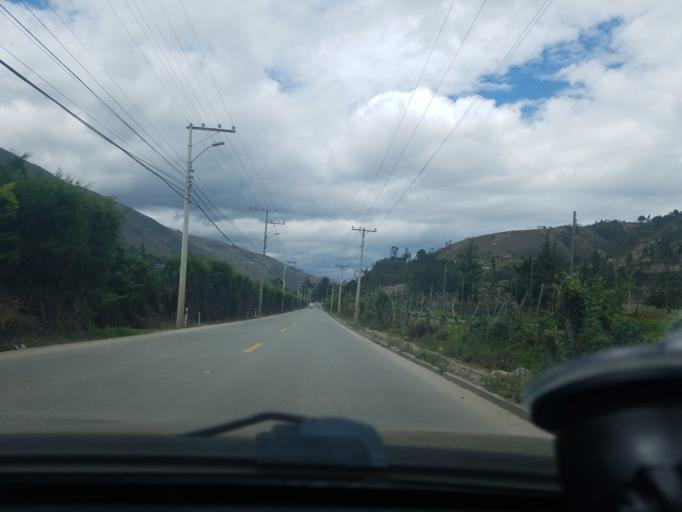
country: EC
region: Azuay
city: La Union
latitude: -2.8136
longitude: -78.7734
